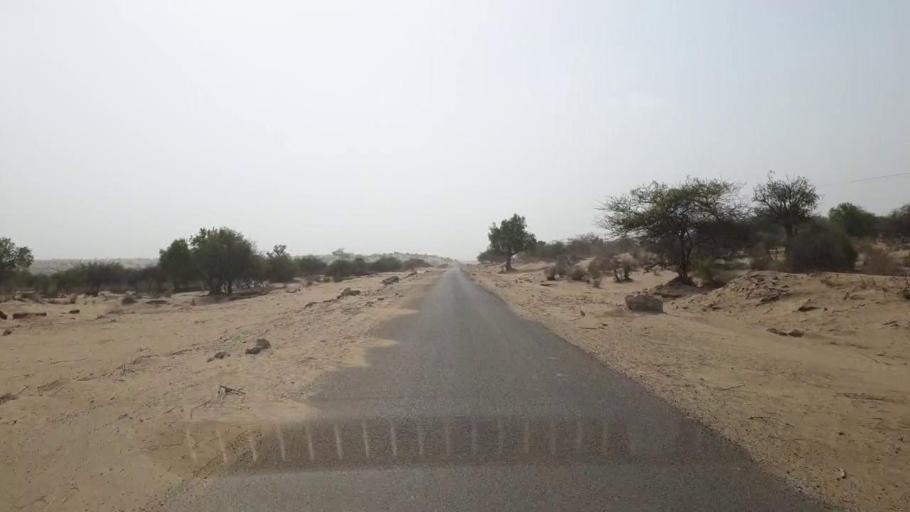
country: PK
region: Sindh
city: Mithi
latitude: 24.6215
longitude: 69.8761
